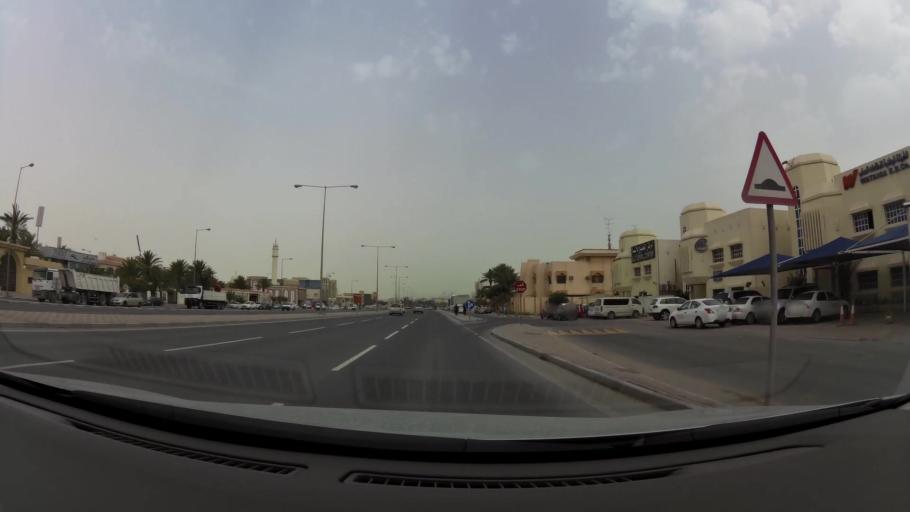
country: QA
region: Baladiyat ad Dawhah
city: Doha
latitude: 25.2559
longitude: 51.5244
